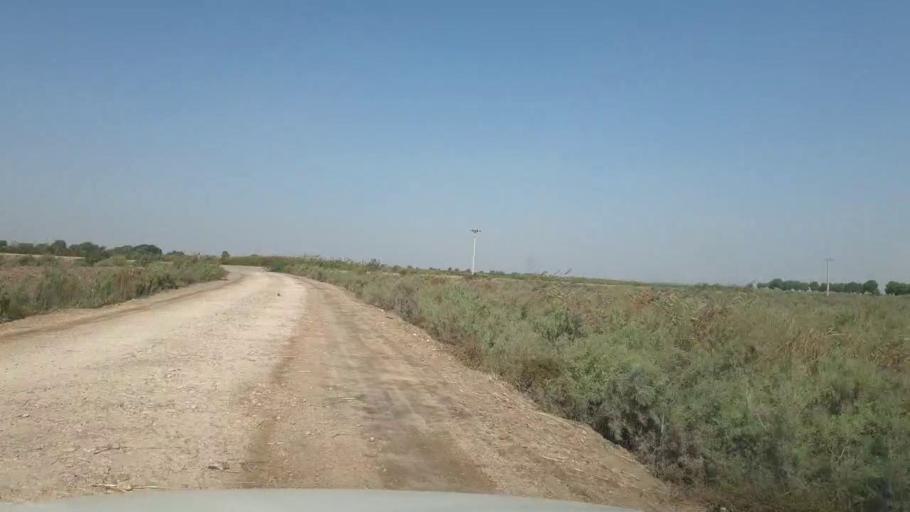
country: PK
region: Sindh
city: Chuhar Jamali
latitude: 24.3820
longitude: 67.8019
